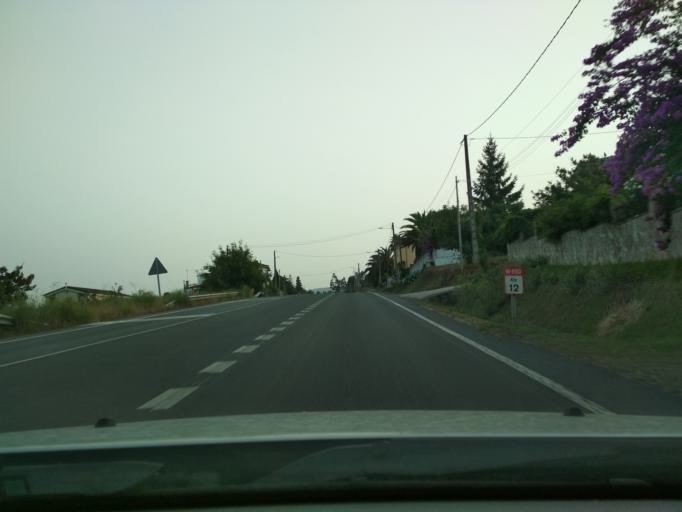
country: ES
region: Galicia
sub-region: Provincia da Coruna
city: Culleredo
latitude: 43.2723
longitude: -8.3668
